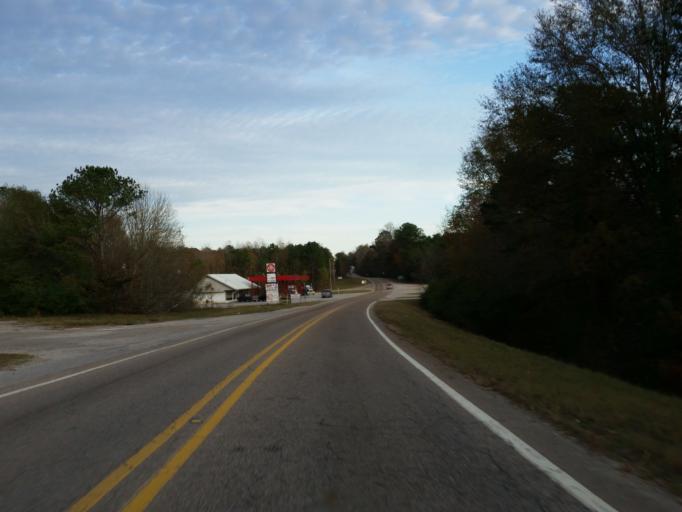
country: US
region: Alabama
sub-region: Sumter County
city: York
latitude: 32.4256
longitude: -88.4499
